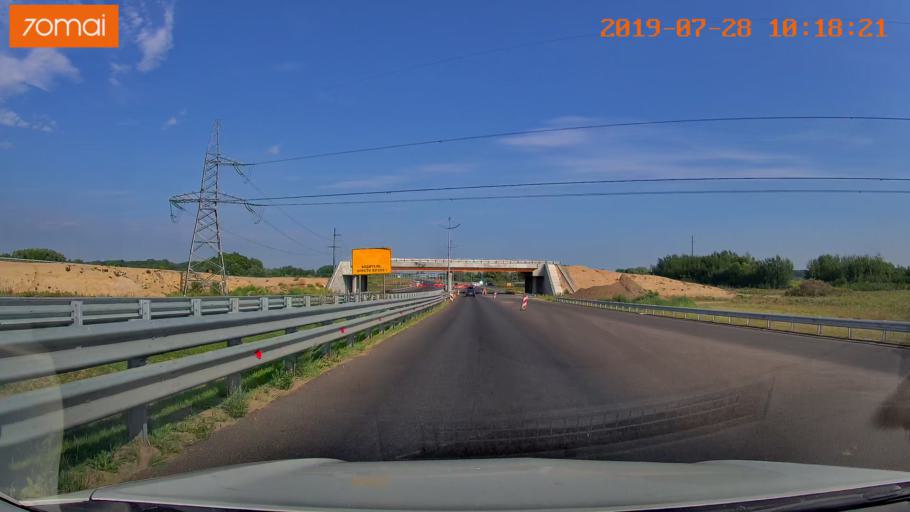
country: RU
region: Kaliningrad
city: Maloye Isakovo
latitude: 54.7511
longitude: 20.5883
